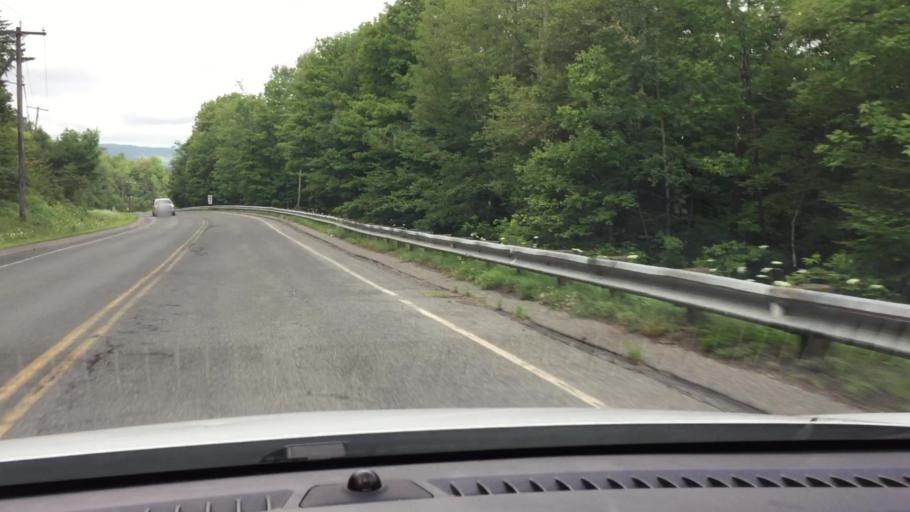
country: US
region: Massachusetts
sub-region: Berkshire County
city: Hinsdale
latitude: 42.4457
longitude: -73.0576
